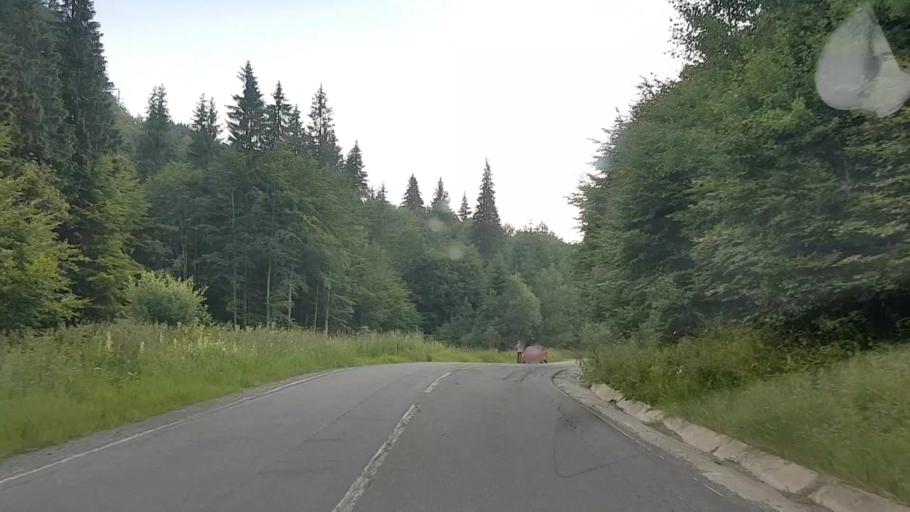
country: RO
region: Harghita
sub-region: Comuna Praid
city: Ocna de Sus
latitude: 46.6239
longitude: 25.2537
